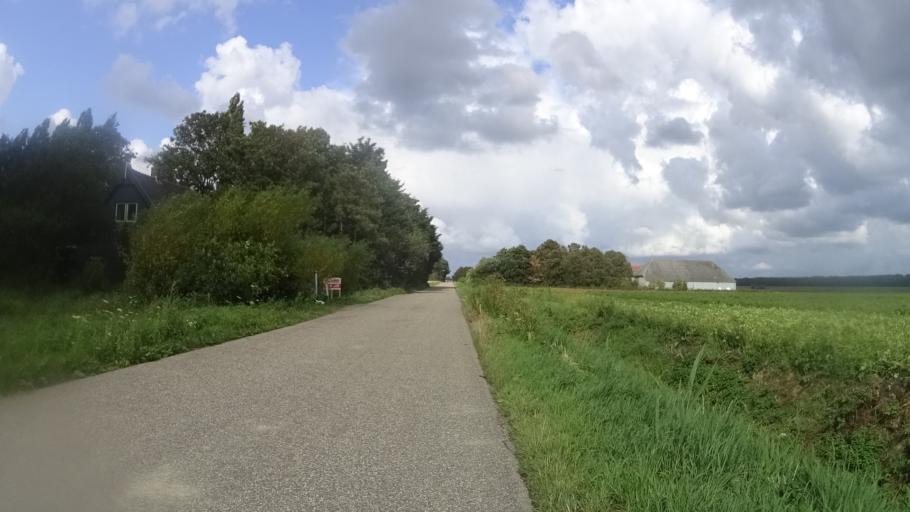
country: NL
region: North Holland
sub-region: Gemeente Schagen
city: Schagen
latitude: 52.8509
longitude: 4.8821
